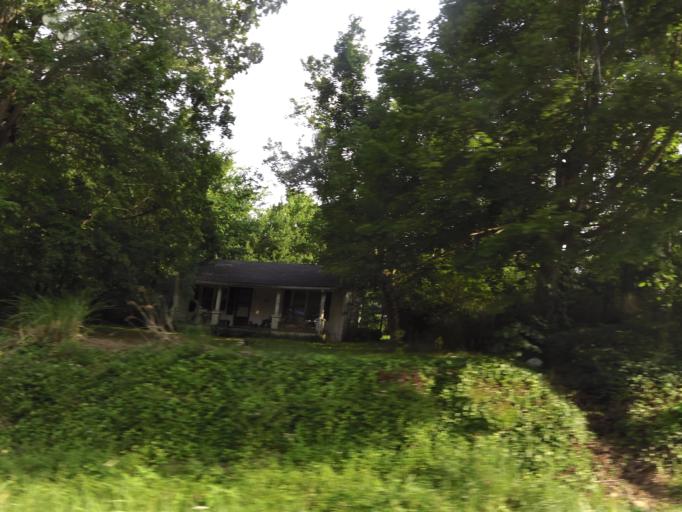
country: US
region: Tennessee
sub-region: Humphreys County
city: McEwen
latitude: 36.1039
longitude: -87.6840
